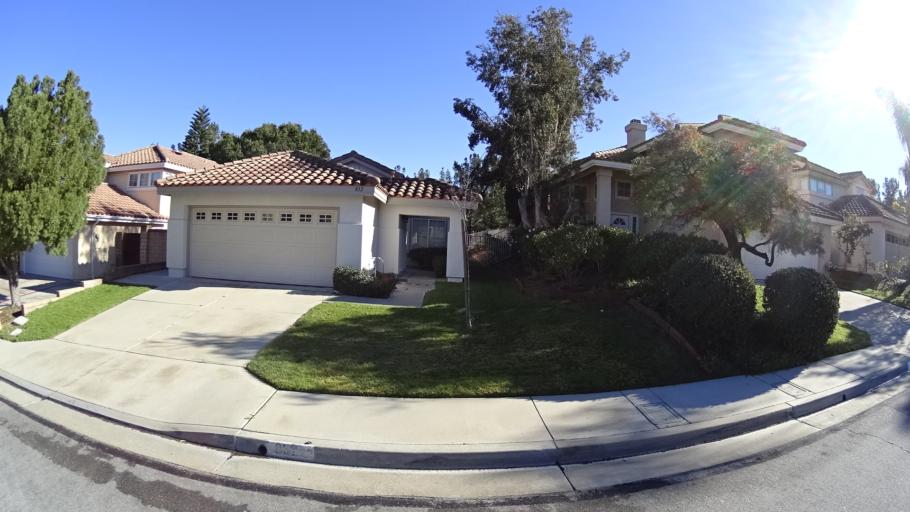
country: US
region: California
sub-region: Orange County
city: Yorba Linda
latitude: 33.8598
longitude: -117.7361
